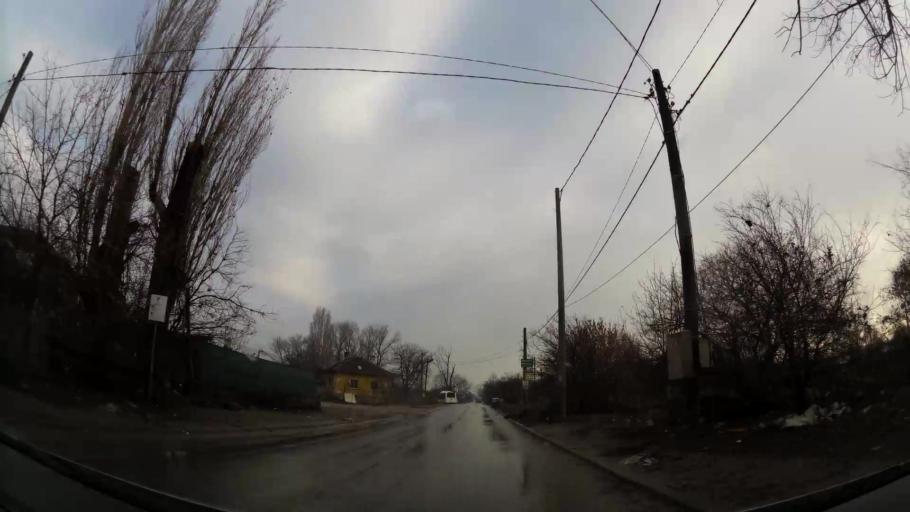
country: BG
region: Sofia-Capital
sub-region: Stolichna Obshtina
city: Sofia
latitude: 42.7185
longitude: 23.3592
